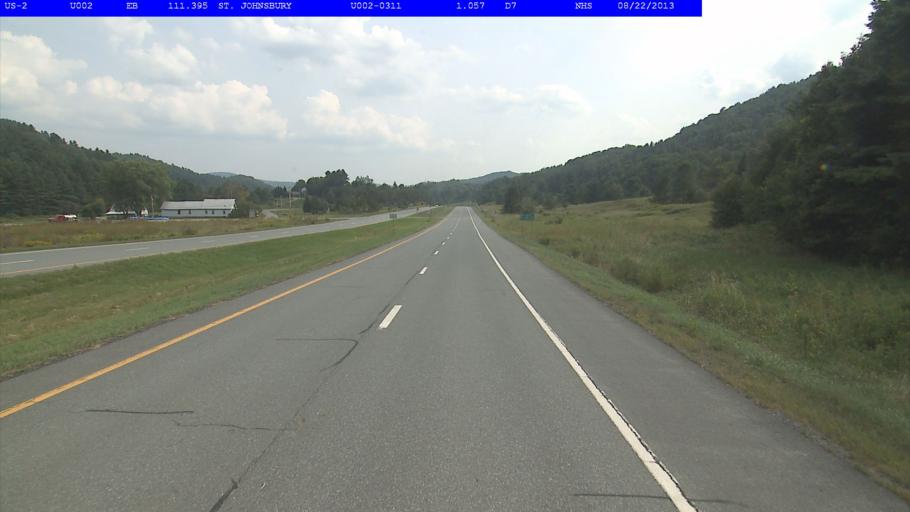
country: US
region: Vermont
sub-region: Caledonia County
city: St Johnsbury
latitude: 44.4394
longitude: -72.0428
